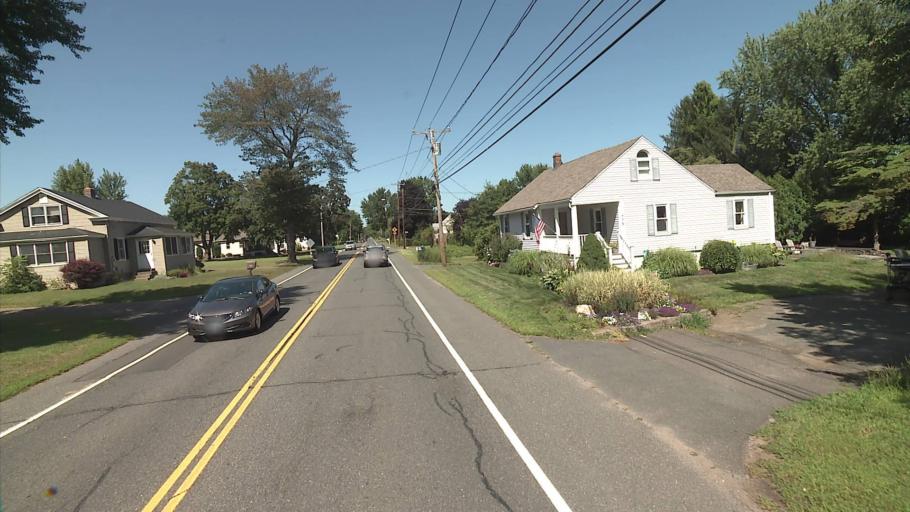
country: US
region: Connecticut
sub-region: Hartford County
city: Thompsonville
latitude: 41.9986
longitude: -72.6143
